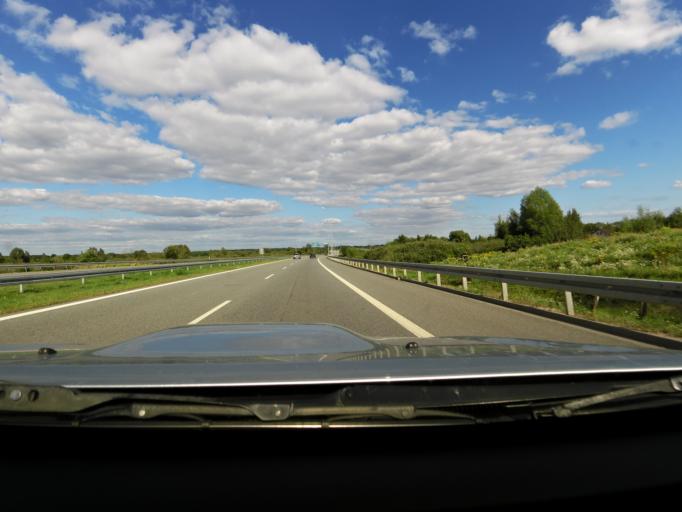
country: PL
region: Warmian-Masurian Voivodeship
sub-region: Powiat elcki
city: Elk
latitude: 53.8450
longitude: 22.3606
